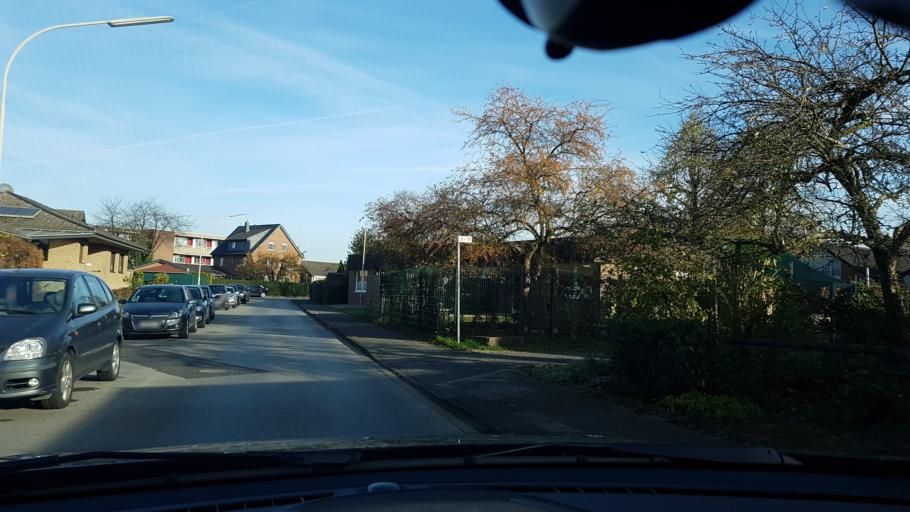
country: DE
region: North Rhine-Westphalia
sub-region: Regierungsbezirk Dusseldorf
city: Grevenbroich
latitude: 51.0797
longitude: 6.6028
